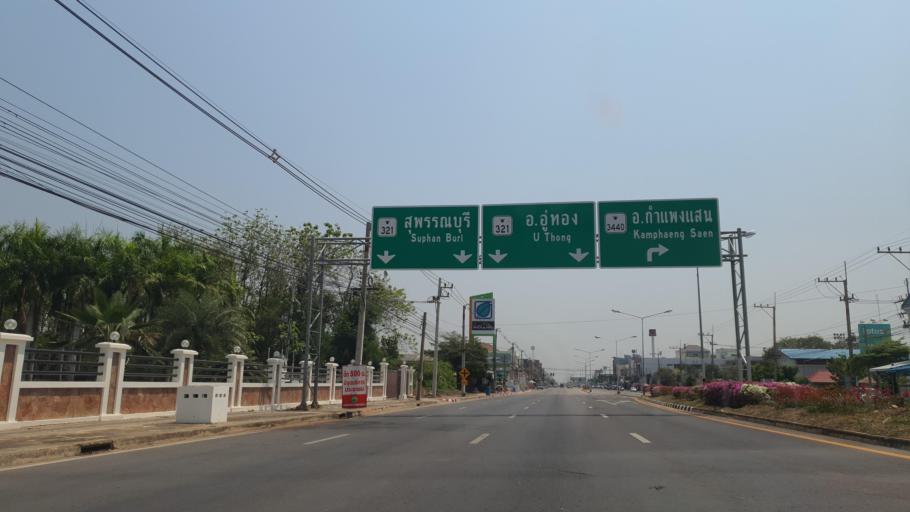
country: TH
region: Suphan Buri
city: U Thong
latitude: 14.2528
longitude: 99.8187
